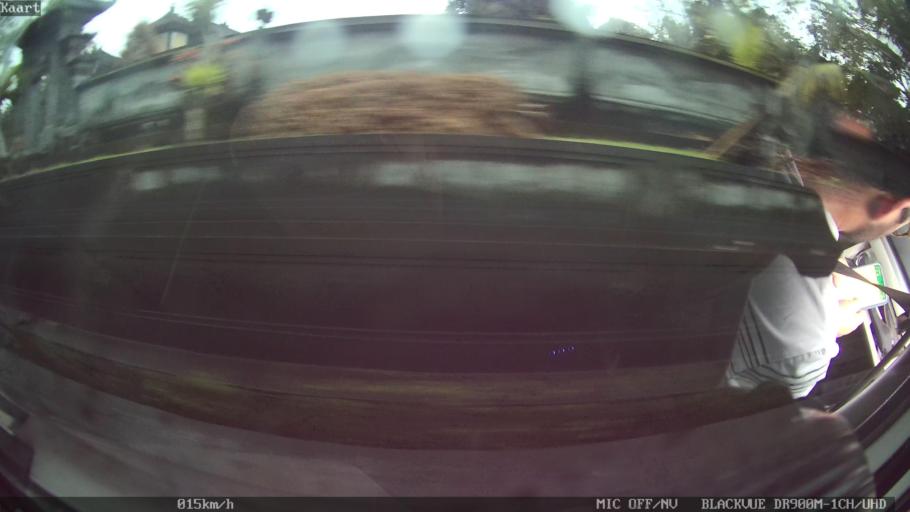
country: ID
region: Bali
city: Banjar Tengah
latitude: -8.4979
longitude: 115.1882
